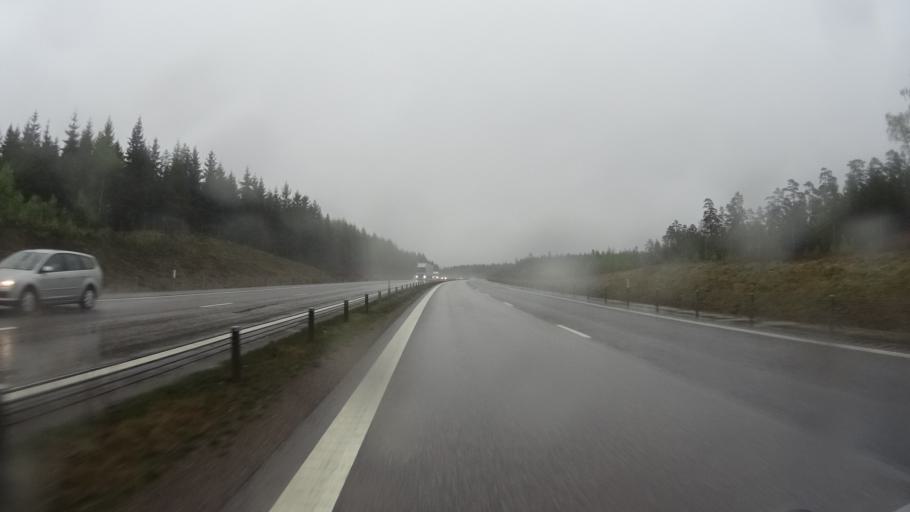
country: SE
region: Kronoberg
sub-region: Markaryds Kommun
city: Markaryd
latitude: 56.4876
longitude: 13.6493
